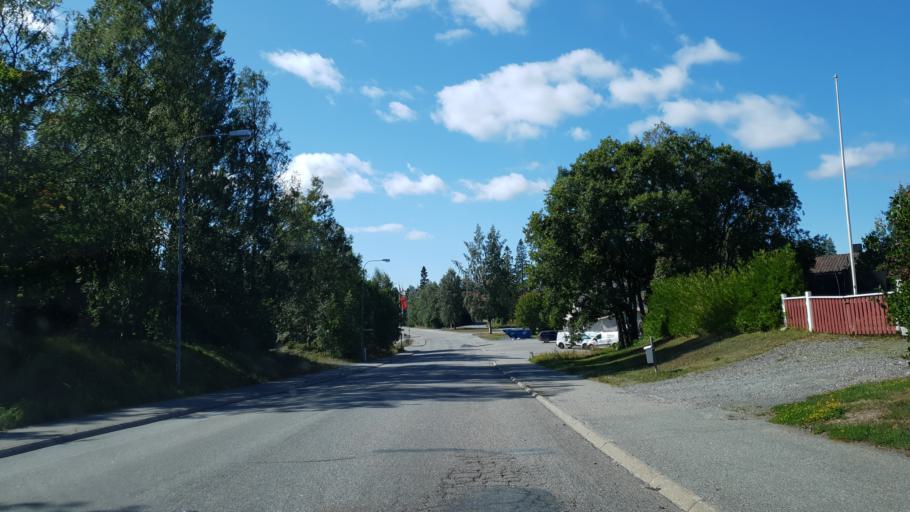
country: SE
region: Vaesterbotten
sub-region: Umea Kommun
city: Holmsund
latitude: 63.7119
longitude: 20.3746
